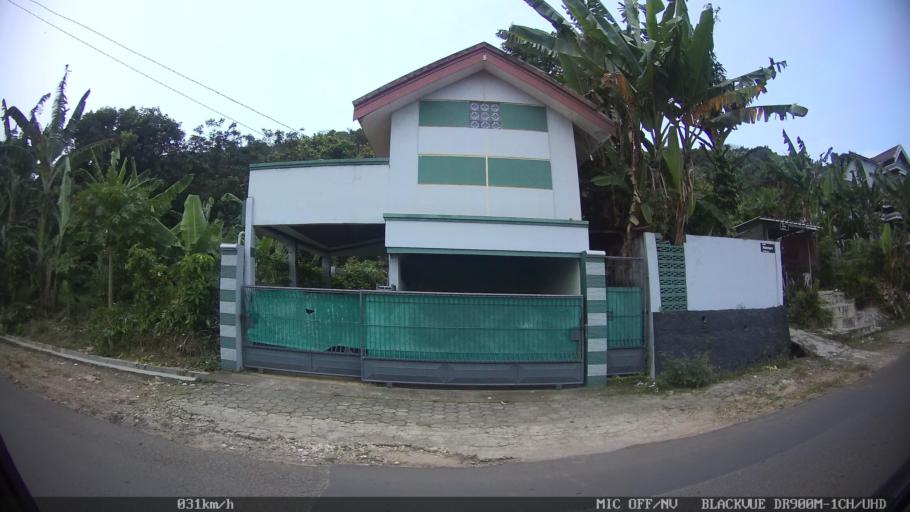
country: ID
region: Lampung
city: Bandarlampung
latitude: -5.4268
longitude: 105.2788
